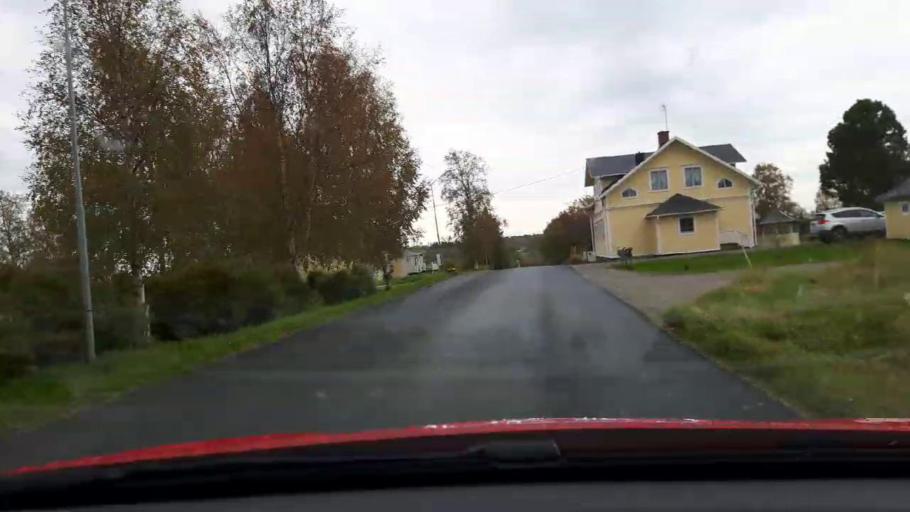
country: SE
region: Jaemtland
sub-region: Bergs Kommun
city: Hoverberg
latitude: 62.9182
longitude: 14.5201
